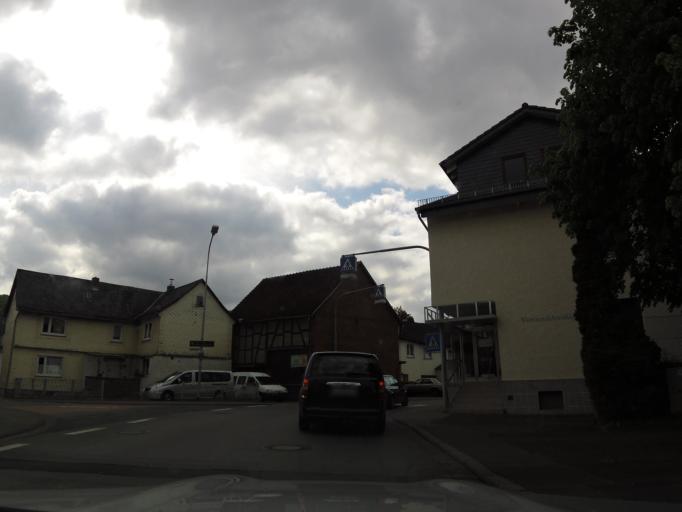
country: DE
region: Hesse
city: Albshausen
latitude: 50.5438
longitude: 8.4368
